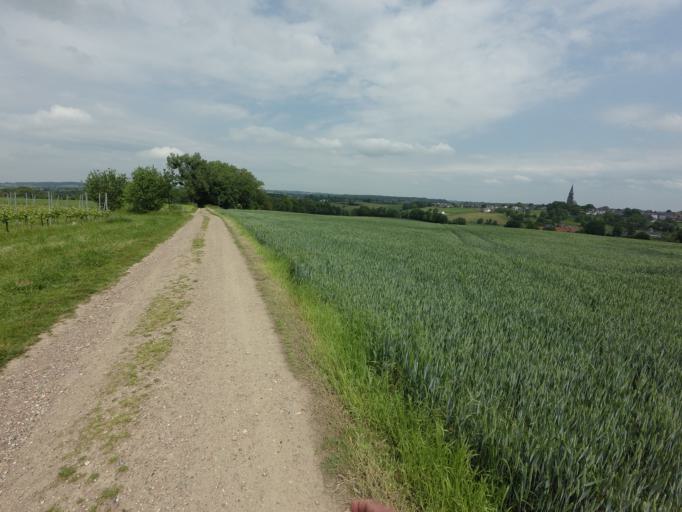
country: BE
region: Wallonia
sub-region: Province de Liege
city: Plombieres
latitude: 50.7843
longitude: 5.9536
